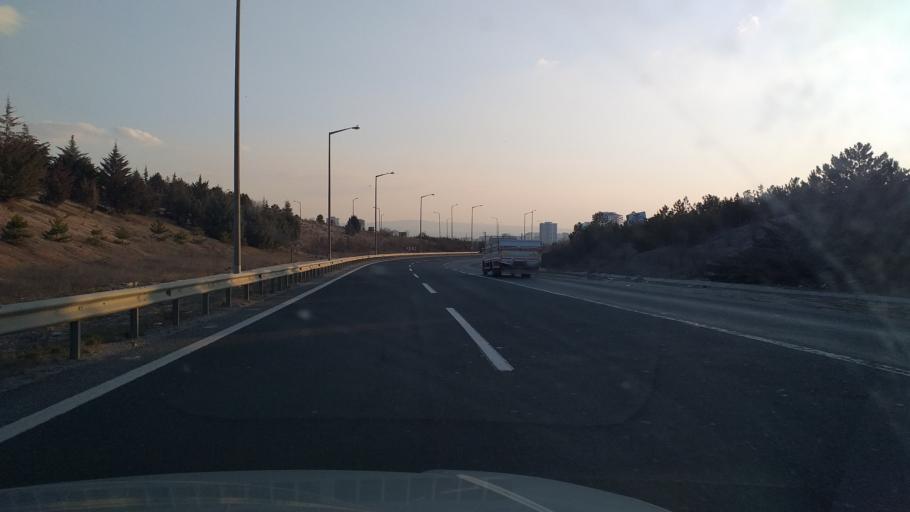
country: TR
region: Ankara
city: Etimesgut
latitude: 40.0242
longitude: 32.6428
